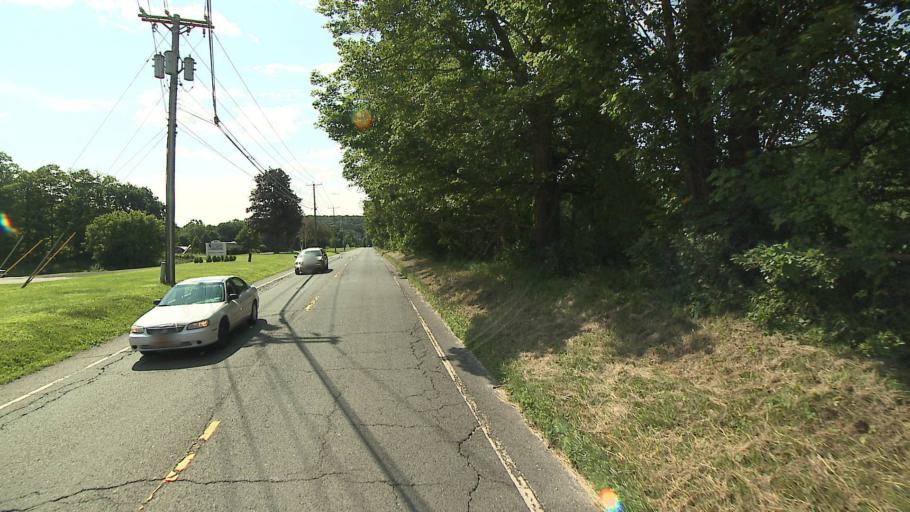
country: US
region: Connecticut
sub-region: Litchfield County
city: New Milford
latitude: 41.5890
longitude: -73.4476
